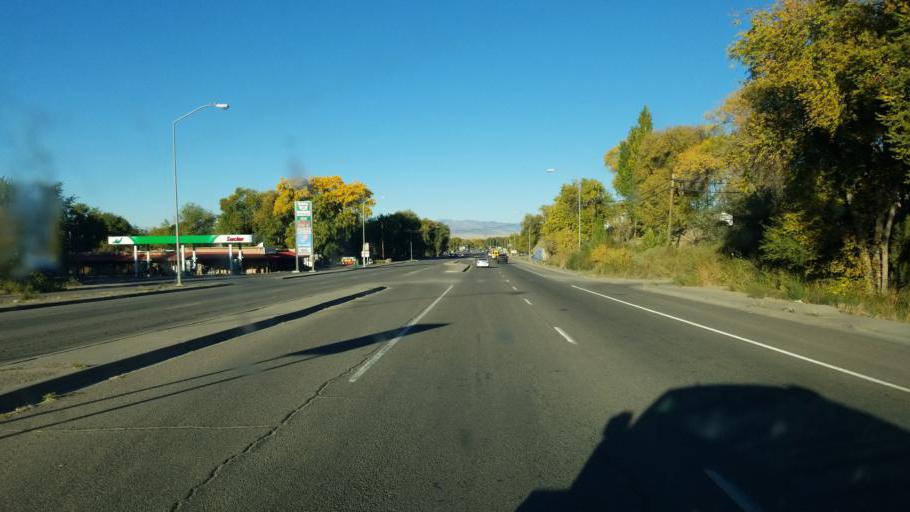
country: US
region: New Mexico
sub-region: San Juan County
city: Shiprock
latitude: 36.7844
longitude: -108.6741
